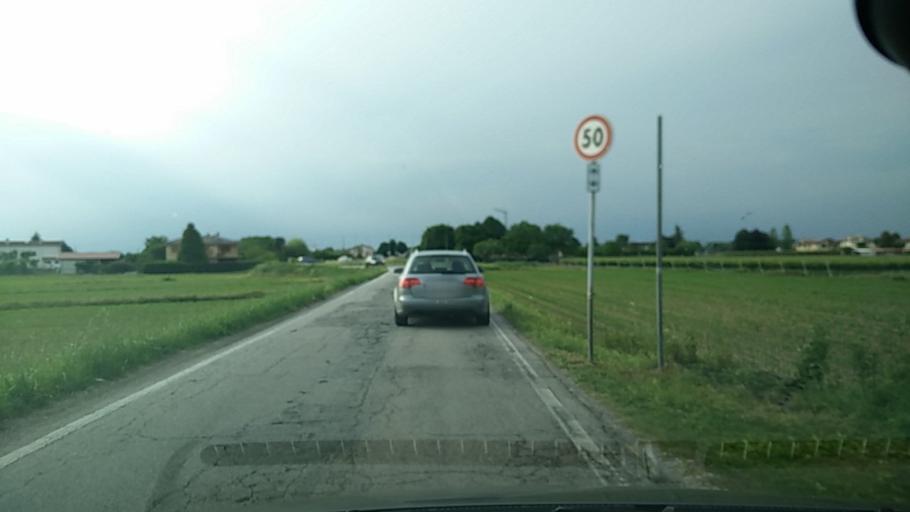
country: IT
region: Veneto
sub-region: Provincia di Venezia
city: Passarella
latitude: 45.5904
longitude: 12.5990
